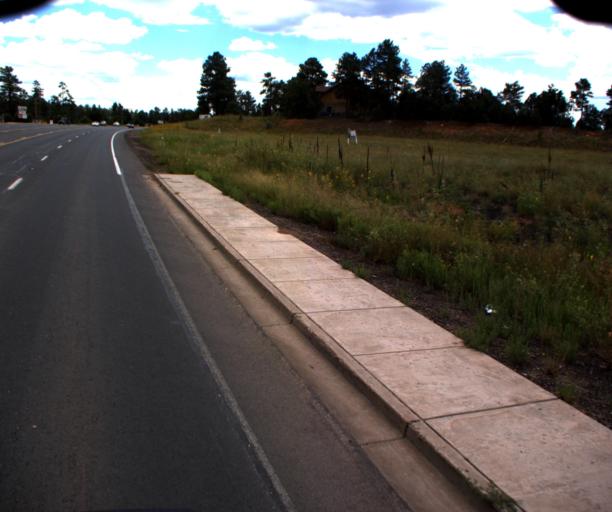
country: US
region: Arizona
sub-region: Navajo County
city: Show Low
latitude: 34.2094
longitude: -110.0239
